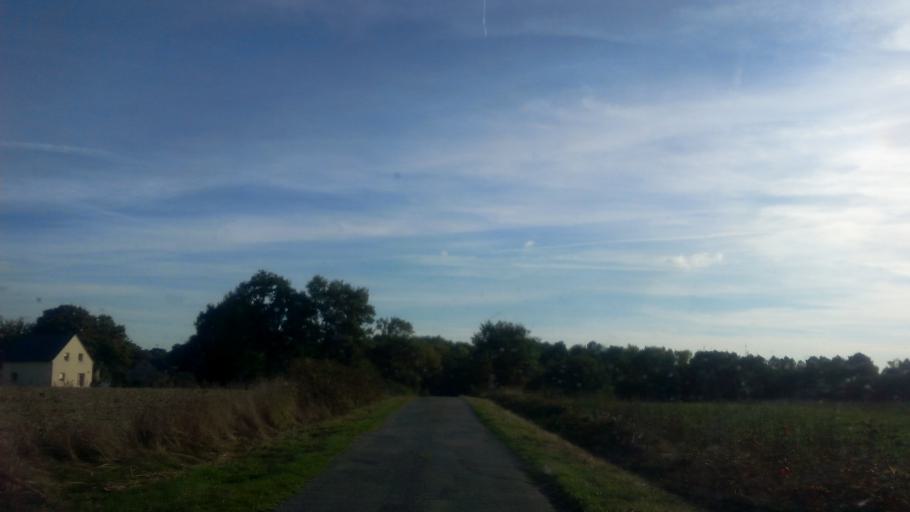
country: FR
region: Brittany
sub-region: Departement du Morbihan
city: Saint-Vincent-sur-Oust
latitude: 47.7051
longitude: -2.1123
